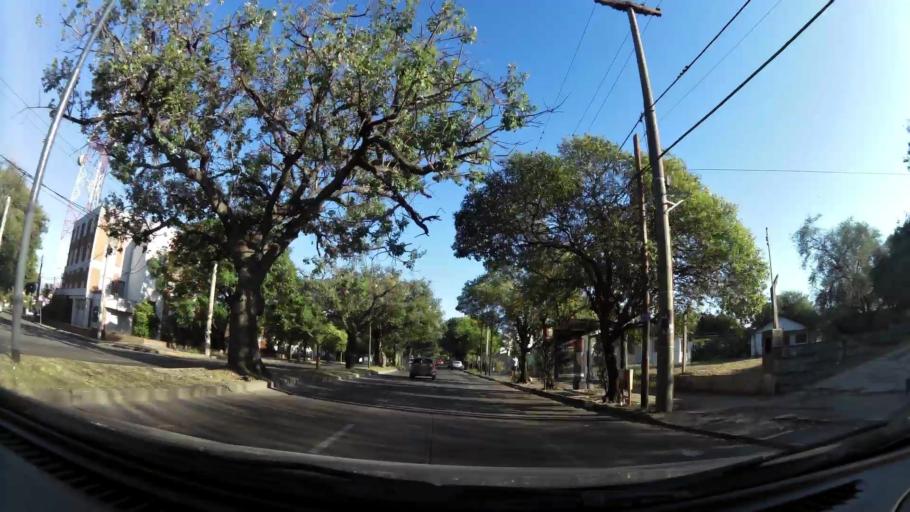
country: AR
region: Cordoba
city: Villa Allende
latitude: -31.3479
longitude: -64.2495
